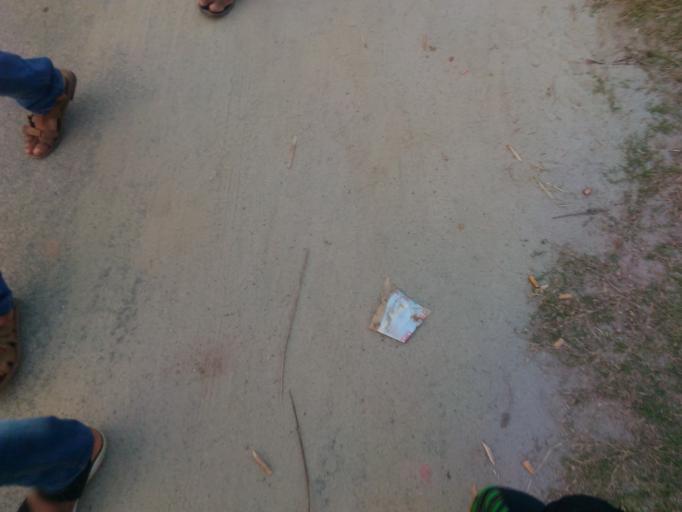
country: BD
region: Dhaka
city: Tungi
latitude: 23.8461
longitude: 90.3673
